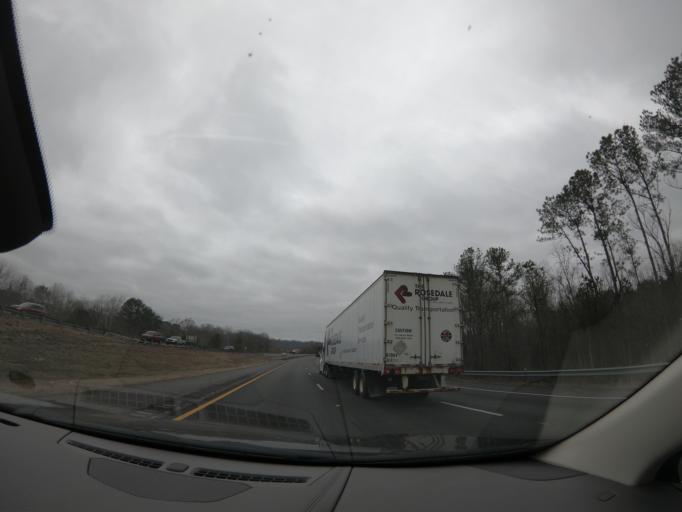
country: US
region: Georgia
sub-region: Catoosa County
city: Indian Springs
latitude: 34.9434
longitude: -85.1706
